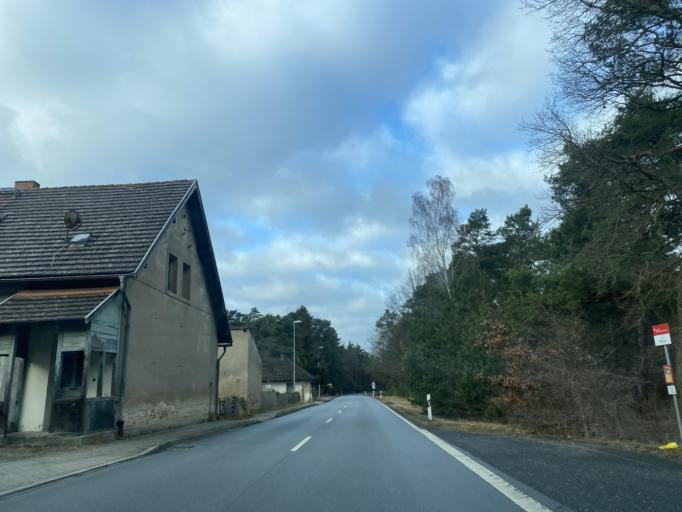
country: DE
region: Saxony
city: Rietschen
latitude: 51.4837
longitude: 14.8462
